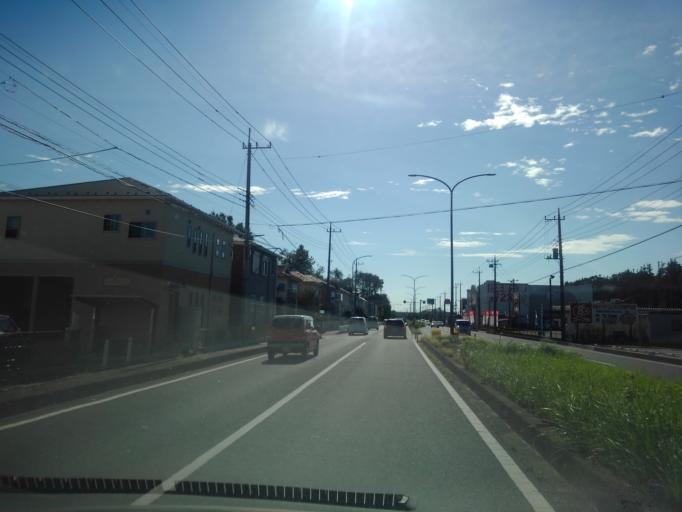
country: JP
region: Saitama
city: Sayama
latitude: 35.8197
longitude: 139.3882
